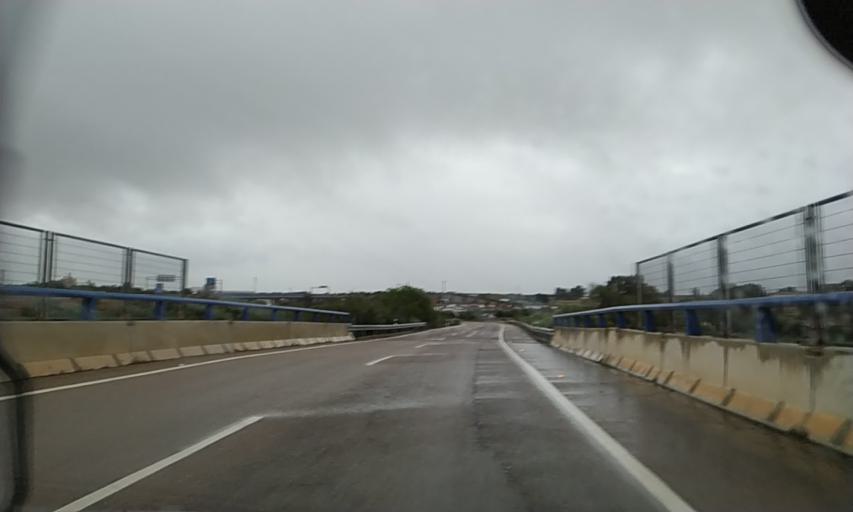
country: ES
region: Extremadura
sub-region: Provincia de Badajoz
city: Calamonte
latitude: 38.9069
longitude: -6.3770
